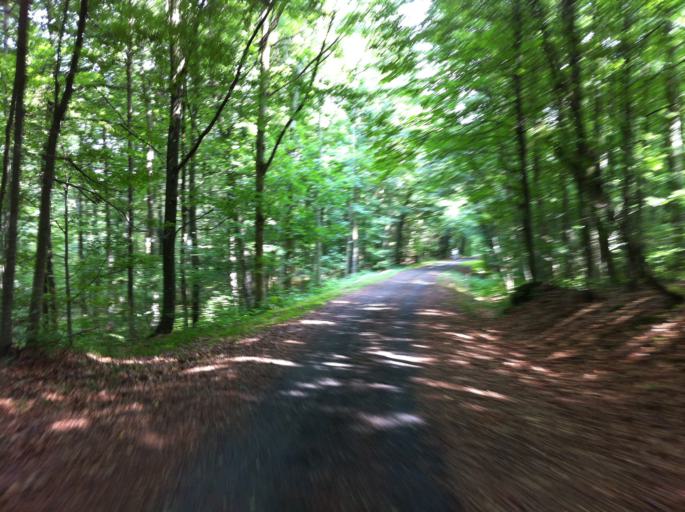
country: SE
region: Skane
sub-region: Hassleholms Kommun
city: Vinslov
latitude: 55.9450
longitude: 13.8479
